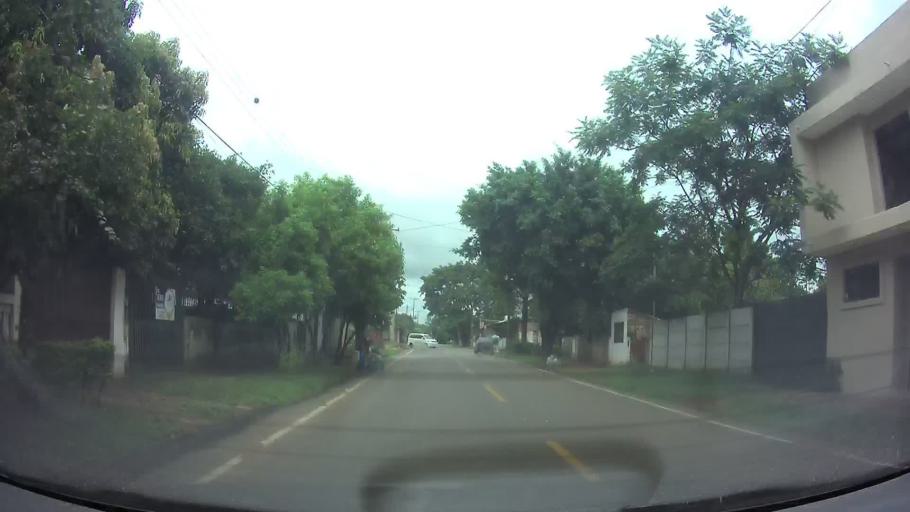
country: PY
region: Central
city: San Lorenzo
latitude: -25.2774
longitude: -57.4868
